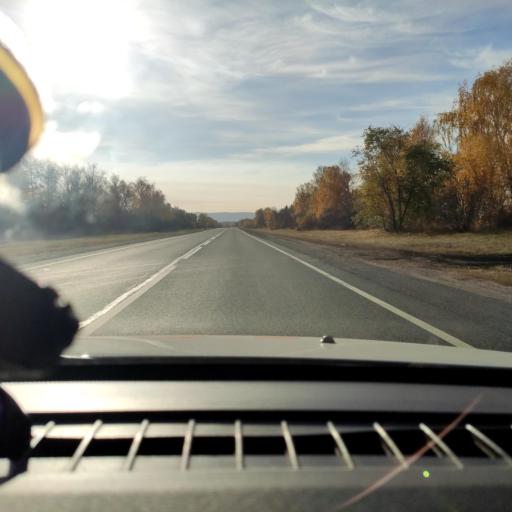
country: RU
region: Samara
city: Volzhskiy
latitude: 53.4755
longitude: 50.1181
